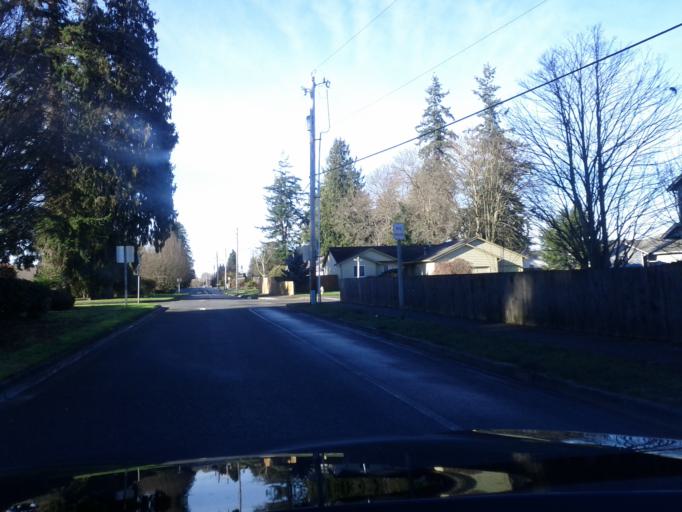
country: US
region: Washington
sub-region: Skagit County
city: Burlington
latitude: 48.4644
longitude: -122.3196
